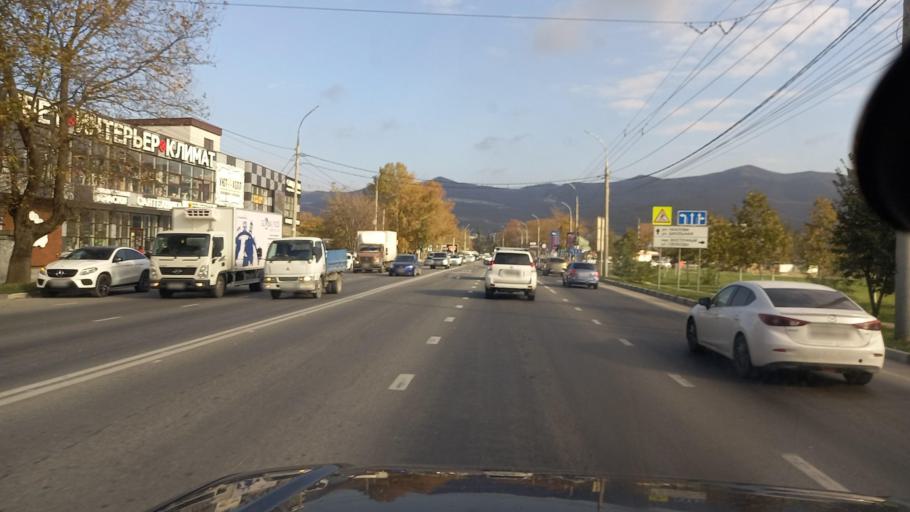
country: RU
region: Krasnodarskiy
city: Gayduk
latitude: 44.7479
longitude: 37.7262
